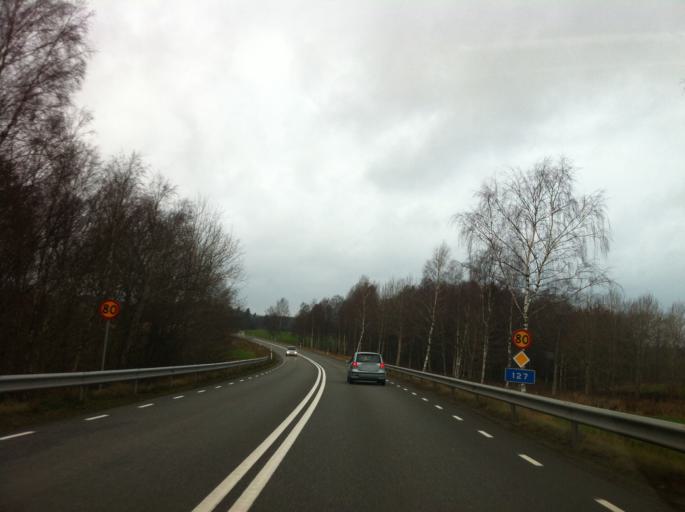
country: SE
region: Joenkoeping
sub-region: Vetlanda Kommun
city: Landsbro
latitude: 57.4035
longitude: 14.9405
